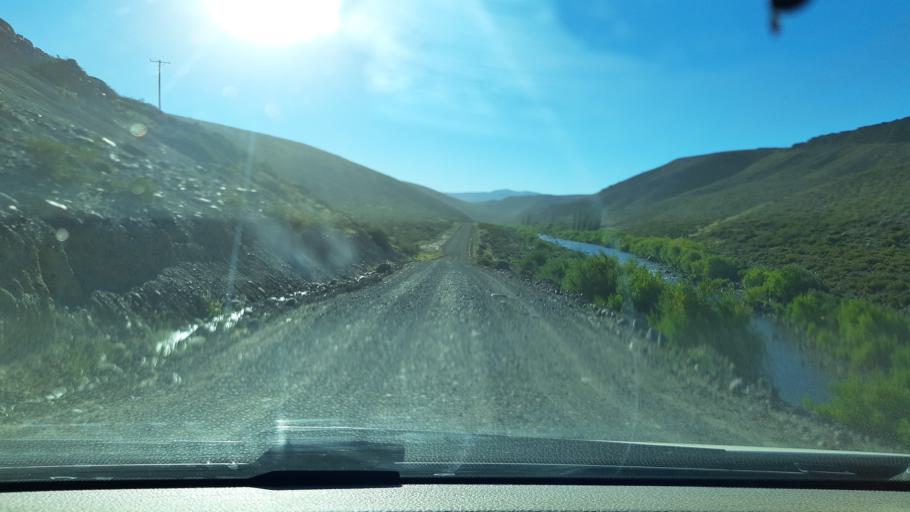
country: AR
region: Neuquen
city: Las Ovejas
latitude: -36.8116
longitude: -70.7057
